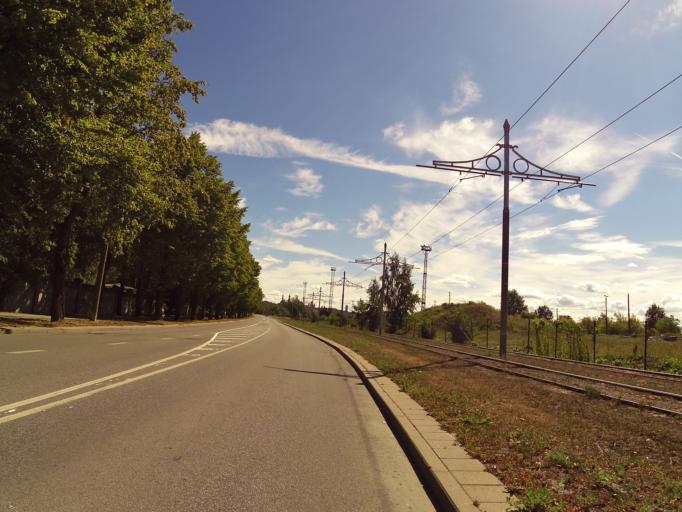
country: EE
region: Harju
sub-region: Tallinna linn
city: Tallinn
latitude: 59.4477
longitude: 24.7132
